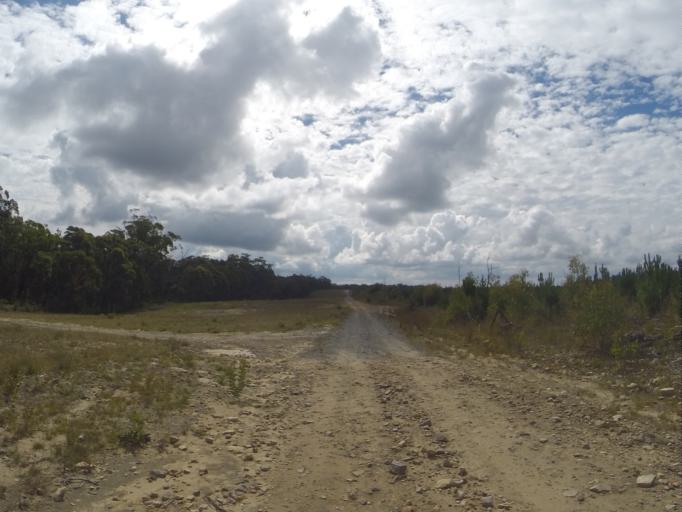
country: AU
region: New South Wales
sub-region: Wingecarribee
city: Moss Vale
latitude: -34.5128
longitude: 150.2273
